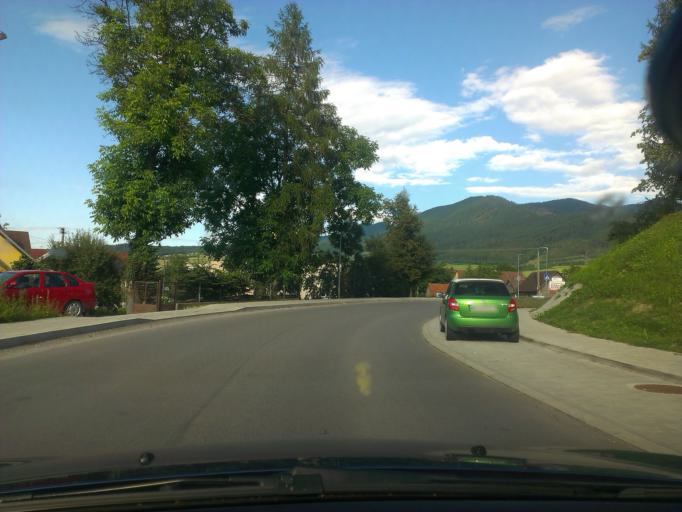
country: SK
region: Zilinsky
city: Krasnany
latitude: 49.1861
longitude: 18.8597
